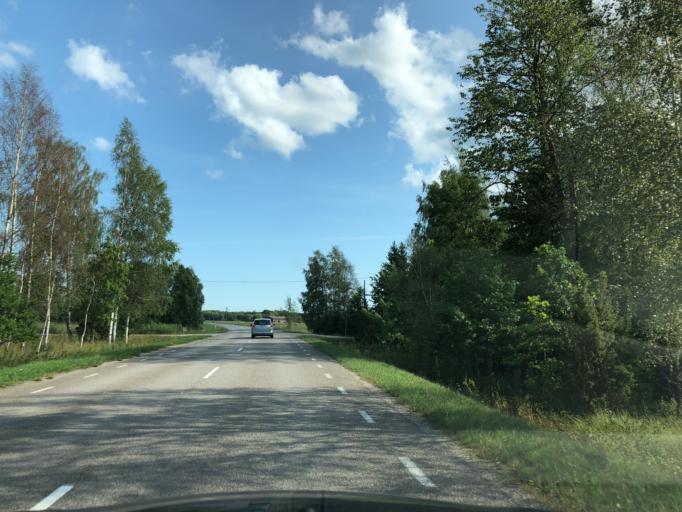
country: EE
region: Hiiumaa
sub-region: Kaerdla linn
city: Kardla
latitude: 58.7148
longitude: 22.5756
